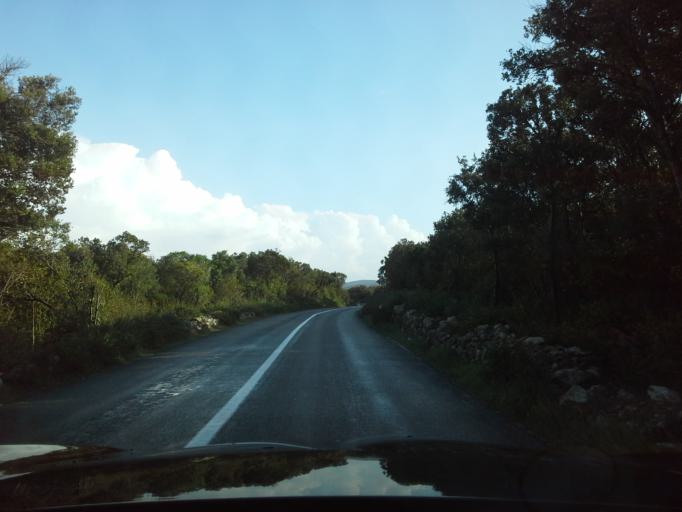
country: HR
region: Primorsko-Goranska
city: Mali Losinj
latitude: 44.6786
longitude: 14.3949
